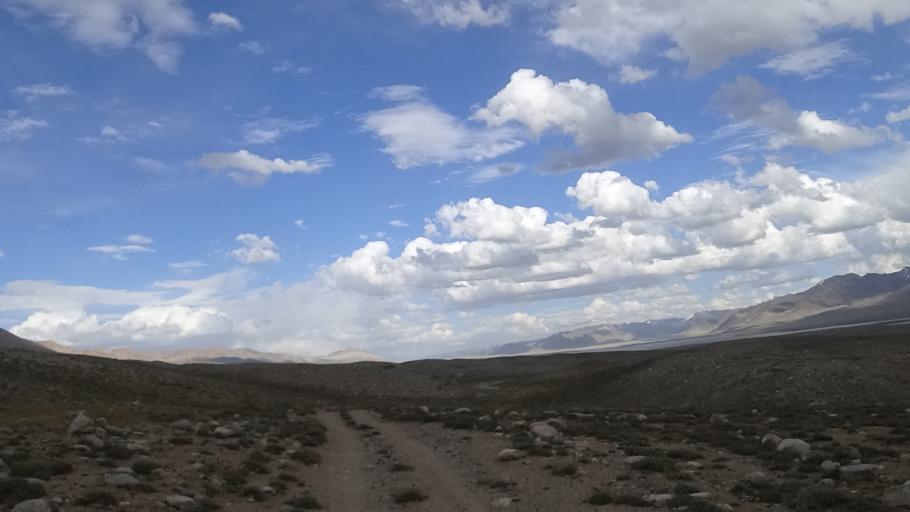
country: TJ
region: Gorno-Badakhshan
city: Murghob
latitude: 37.4689
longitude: 73.5983
